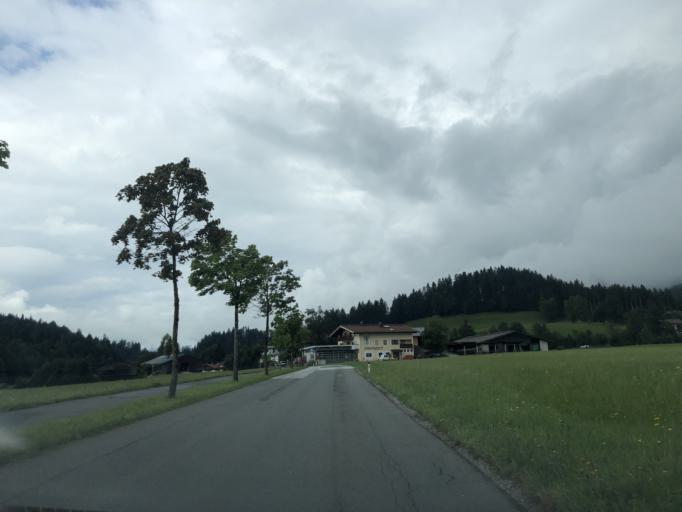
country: AT
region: Tyrol
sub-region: Politischer Bezirk Kitzbuhel
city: Sankt Johann in Tirol
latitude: 47.5225
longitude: 12.4008
